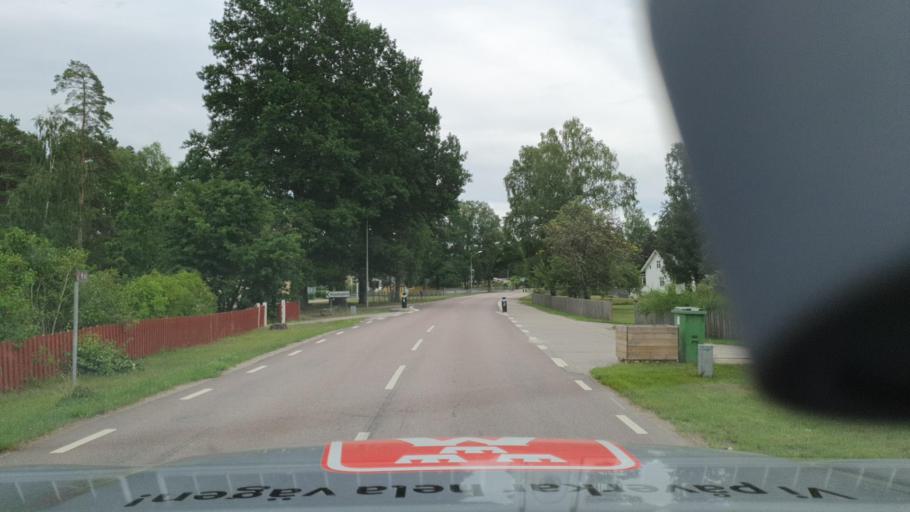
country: SE
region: Kalmar
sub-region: Kalmar Kommun
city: Trekanten
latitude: 56.6247
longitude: 16.0410
